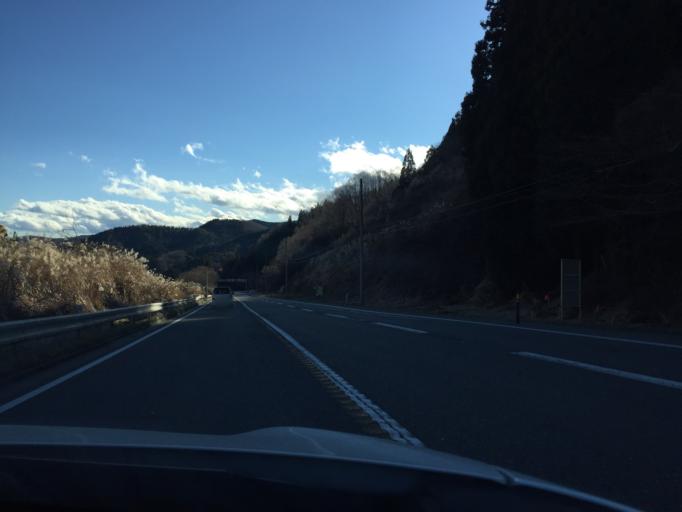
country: JP
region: Fukushima
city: Ishikawa
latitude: 37.1628
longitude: 140.6573
